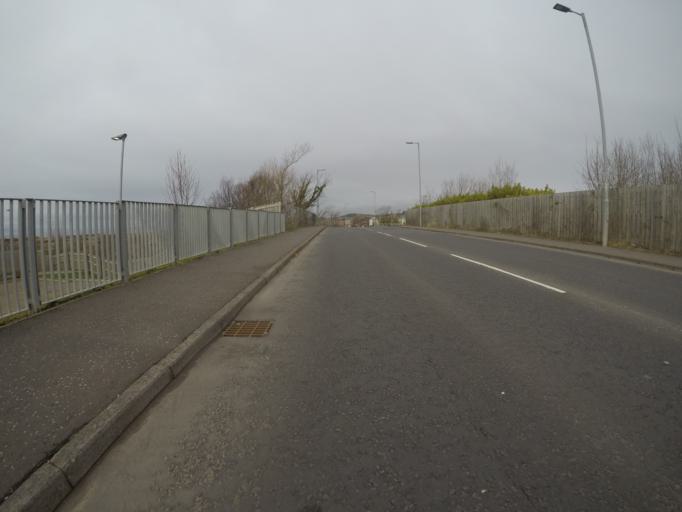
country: GB
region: Scotland
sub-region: North Ayrshire
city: Ardrossan
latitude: 55.6462
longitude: -4.8122
